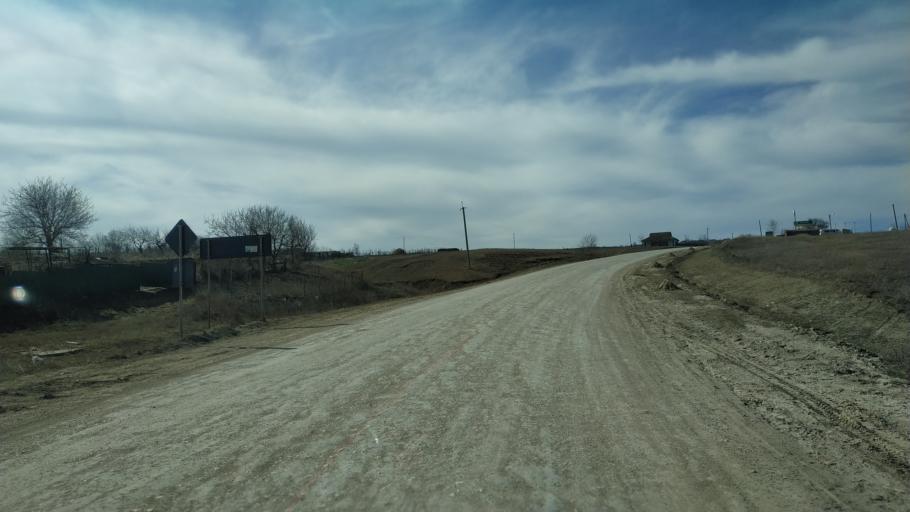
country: MD
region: Nisporeni
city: Nisporeni
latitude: 46.9656
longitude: 28.1828
